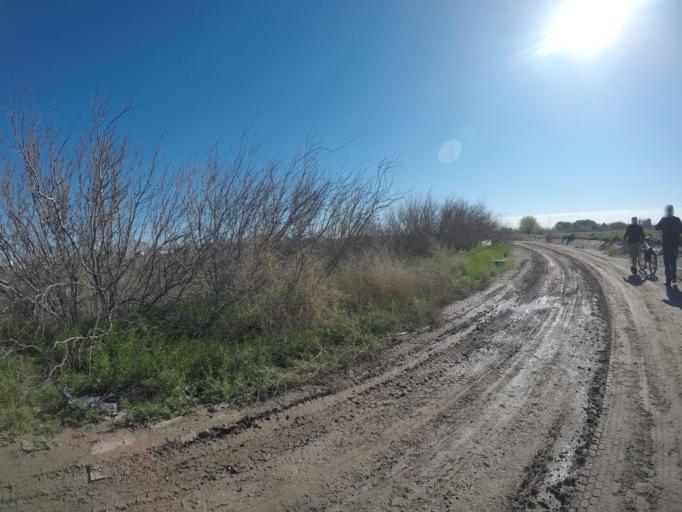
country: US
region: Texas
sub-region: El Paso County
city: Socorro
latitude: 31.6478
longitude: -106.3437
